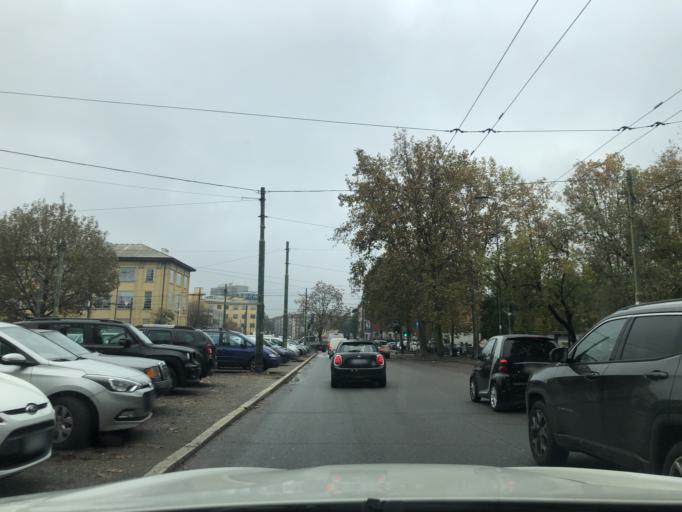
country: IT
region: Lombardy
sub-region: Citta metropolitana di Milano
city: Milano
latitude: 45.4800
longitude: 9.1428
